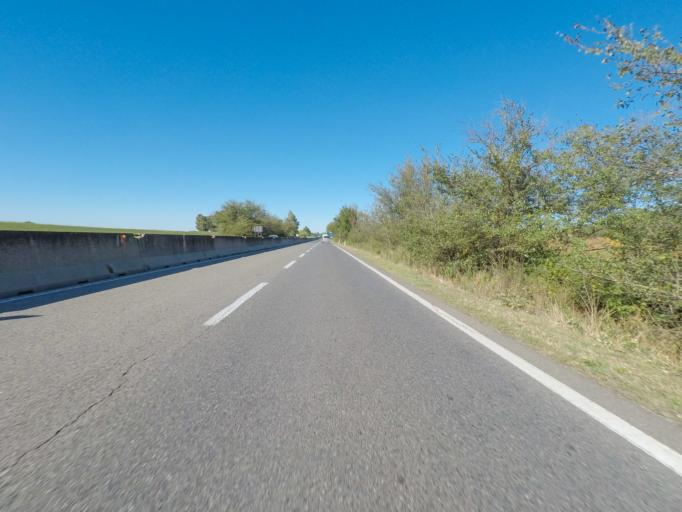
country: IT
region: Tuscany
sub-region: Provincia di Grosseto
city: Grosseto
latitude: 42.6944
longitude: 11.1380
